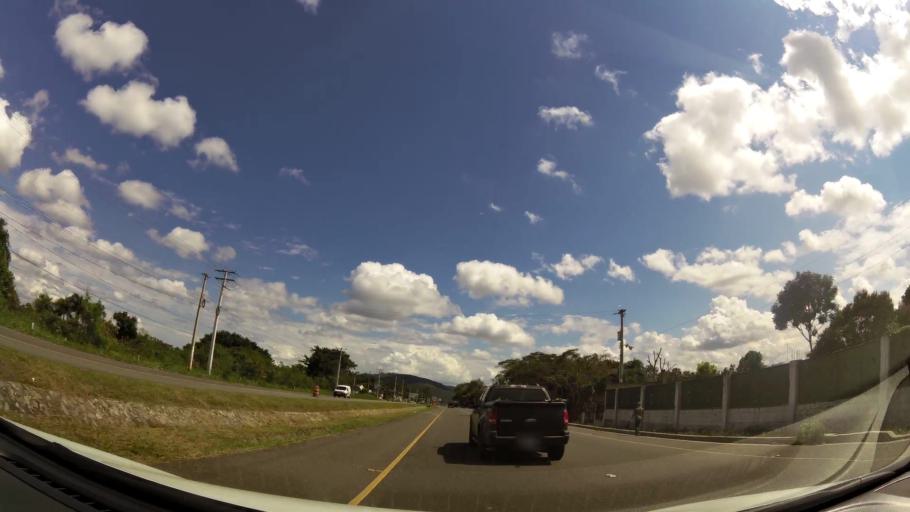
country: DO
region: La Vega
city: Rio Verde Arriba
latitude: 19.3329
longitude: -70.5948
